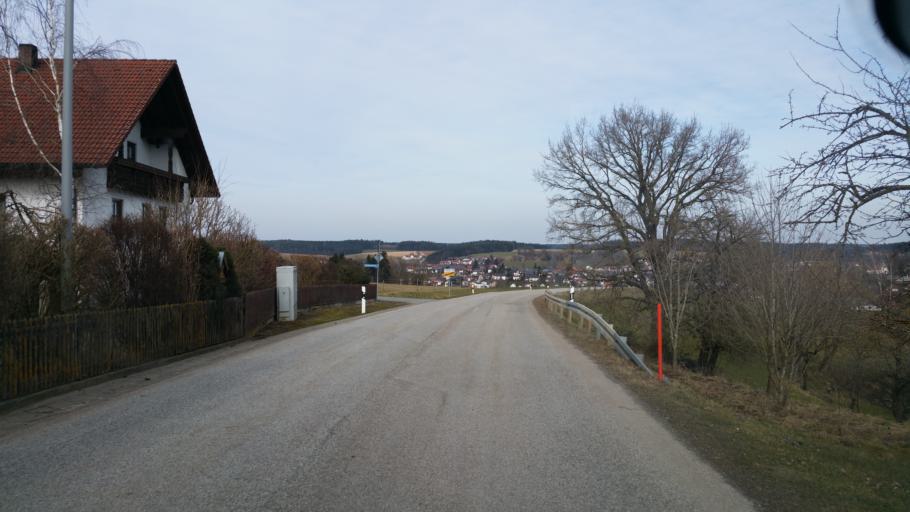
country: DE
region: Bavaria
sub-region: Lower Bavaria
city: Furth
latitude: 48.5801
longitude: 12.0171
